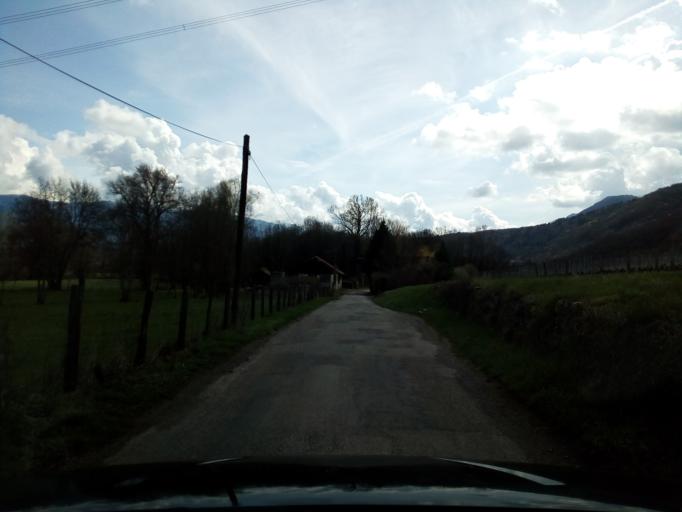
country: FR
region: Rhone-Alpes
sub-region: Departement de l'Isere
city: Chapareillan
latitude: 45.4840
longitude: 5.9826
